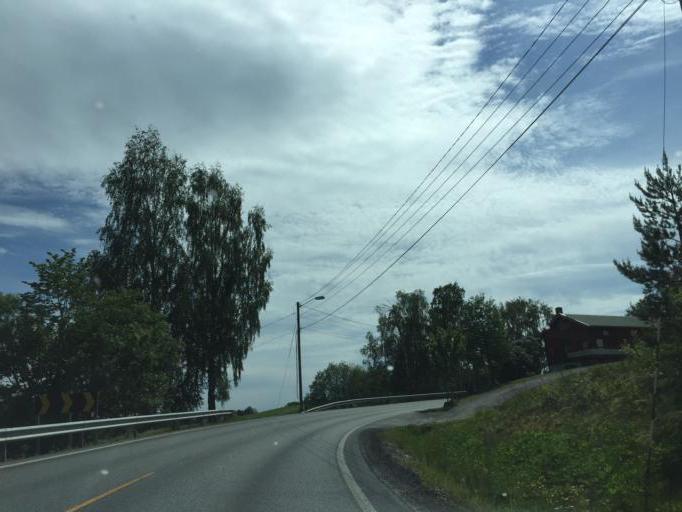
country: NO
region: Akershus
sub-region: Nes
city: Arnes
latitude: 60.1515
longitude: 11.4209
